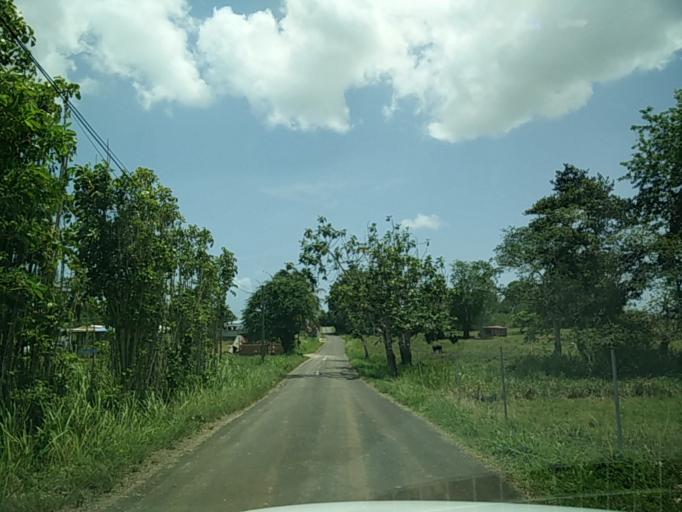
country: GP
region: Guadeloupe
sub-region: Guadeloupe
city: Les Abymes
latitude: 16.2856
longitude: -61.5229
